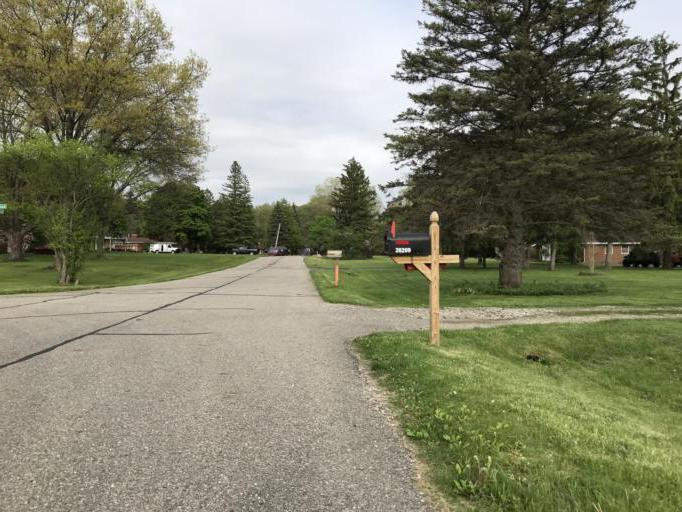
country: US
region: Michigan
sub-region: Oakland County
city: Farmington
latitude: 42.4726
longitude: -83.3270
